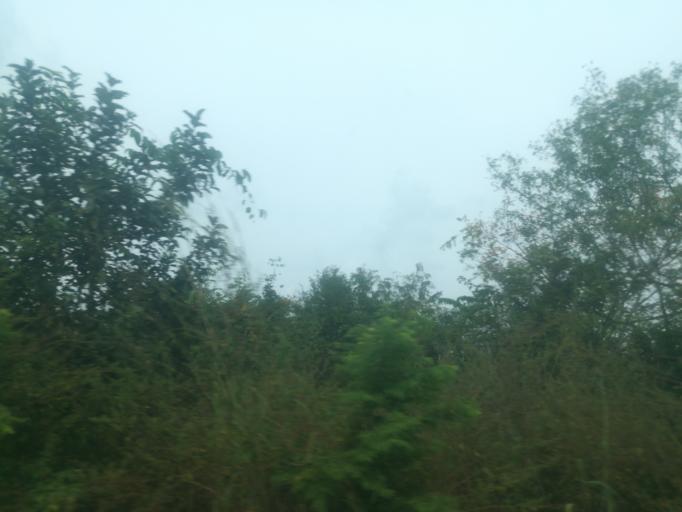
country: NG
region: Ogun
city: Ayetoro
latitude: 7.3468
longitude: 3.0560
